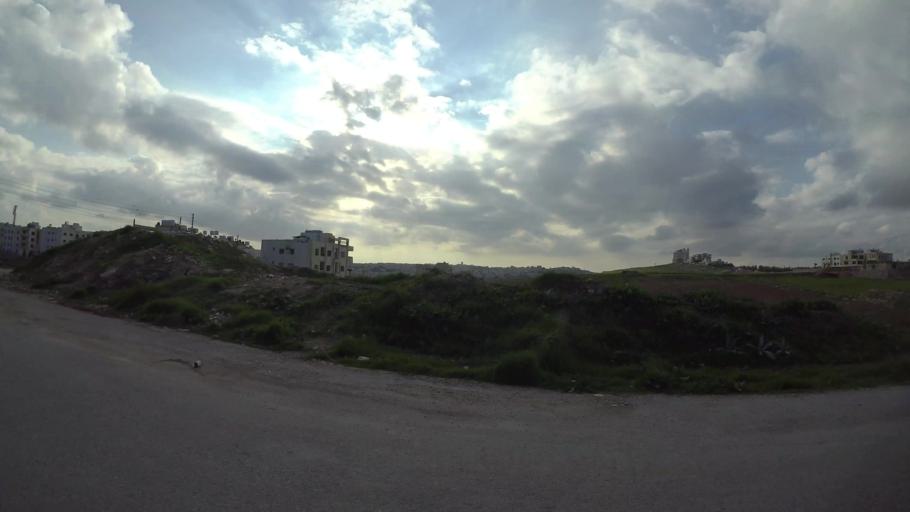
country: JO
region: Amman
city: Al Bunayyat ash Shamaliyah
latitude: 31.9104
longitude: 35.8725
